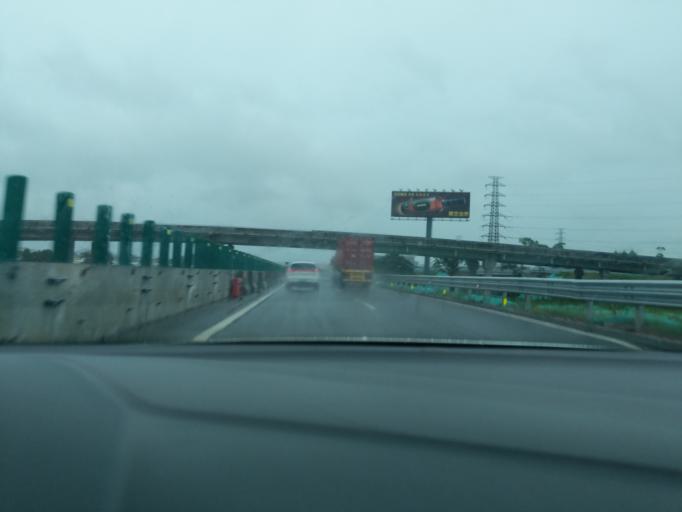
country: CN
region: Guangdong
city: Shuikou
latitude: 22.4711
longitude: 112.7608
